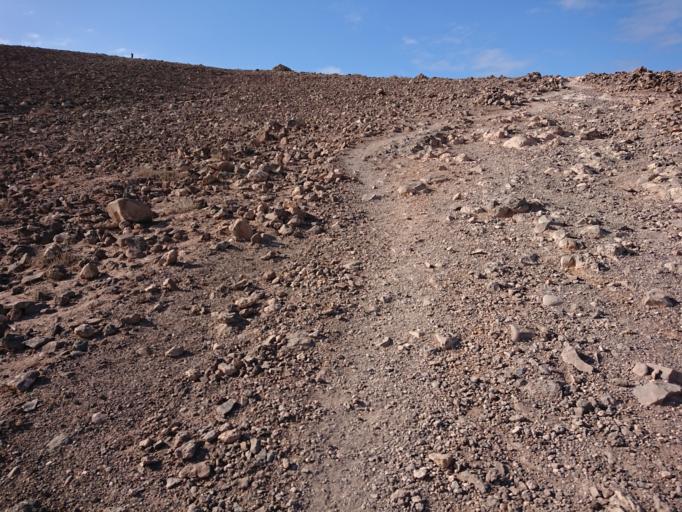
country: ES
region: Canary Islands
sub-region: Provincia de Las Palmas
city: Playa Blanca
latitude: 28.8712
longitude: -13.8519
